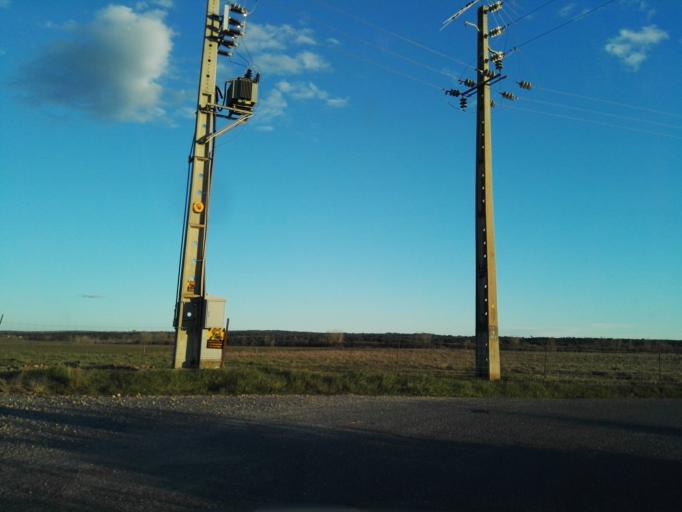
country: PT
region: Castelo Branco
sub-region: Idanha-A-Nova
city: Idanha-a-Nova
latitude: 39.8705
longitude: -7.1358
